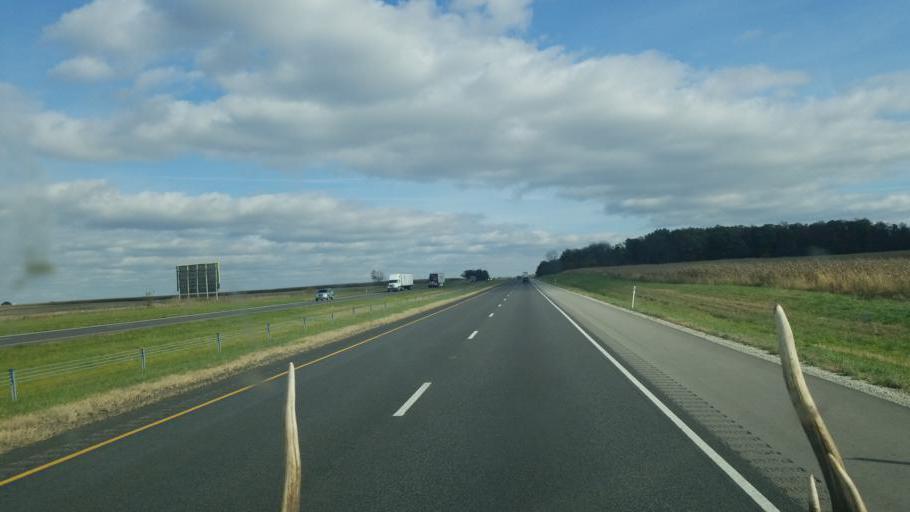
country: US
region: Indiana
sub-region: Wayne County
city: Cambridge City
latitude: 39.8538
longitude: -85.0945
